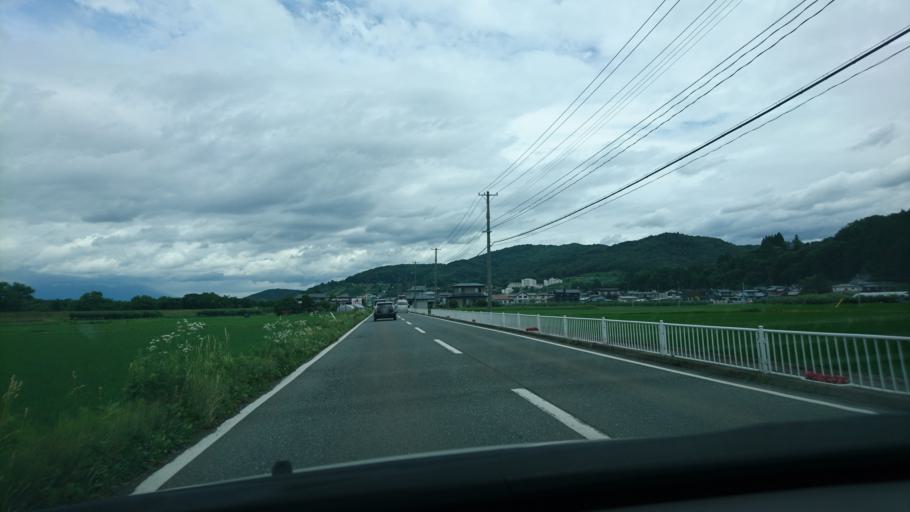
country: JP
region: Iwate
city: Morioka-shi
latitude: 39.6466
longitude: 141.1843
